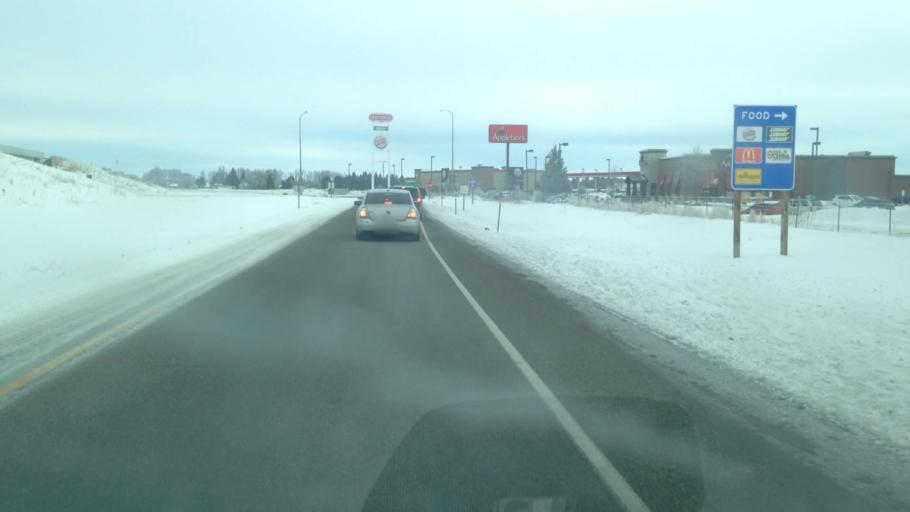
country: US
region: Idaho
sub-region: Madison County
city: Rexburg
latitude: 43.8030
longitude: -111.8130
